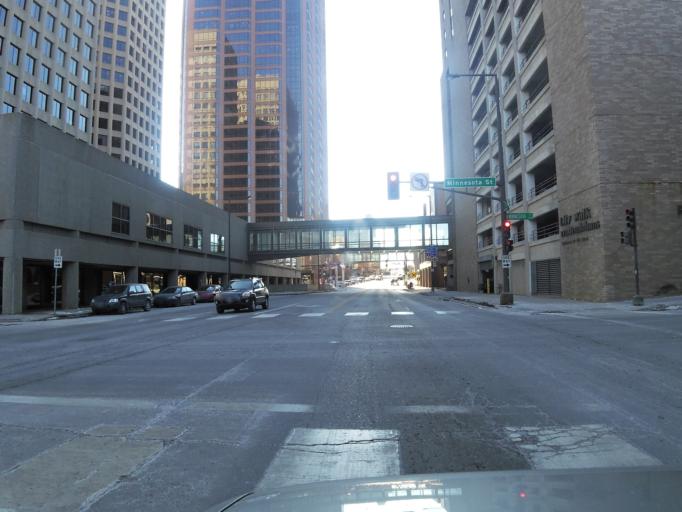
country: US
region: Minnesota
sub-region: Ramsey County
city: Saint Paul
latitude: 44.9493
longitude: -93.0942
